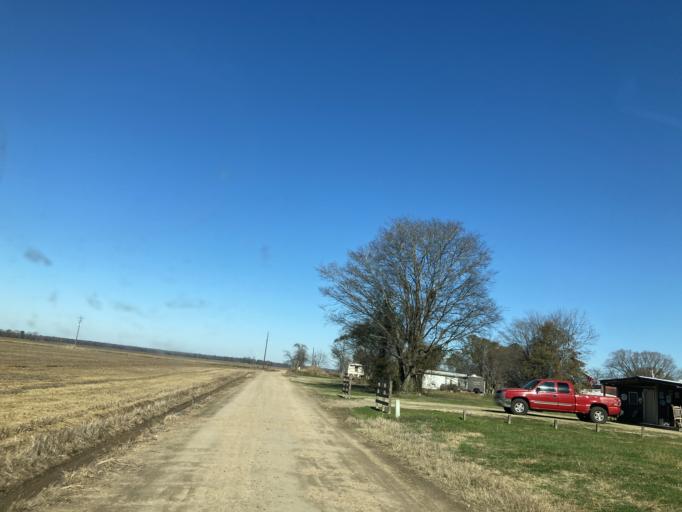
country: US
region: Mississippi
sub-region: Sharkey County
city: Rolling Fork
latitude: 32.8198
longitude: -90.7115
